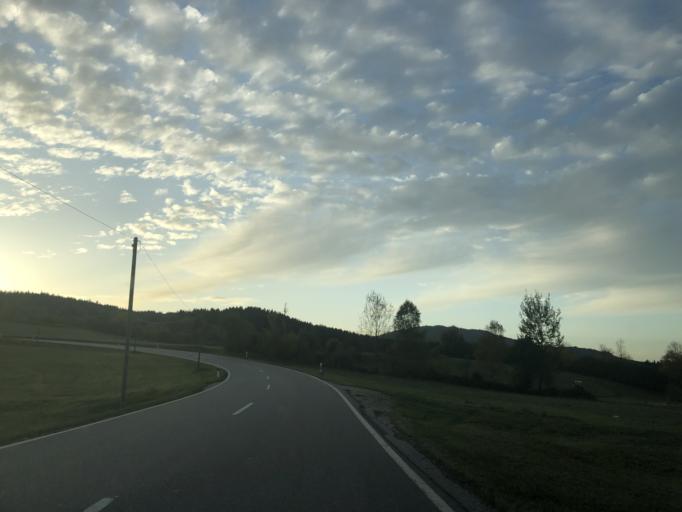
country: DE
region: Bavaria
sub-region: Lower Bavaria
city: Langdorf
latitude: 49.0162
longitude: 13.1571
